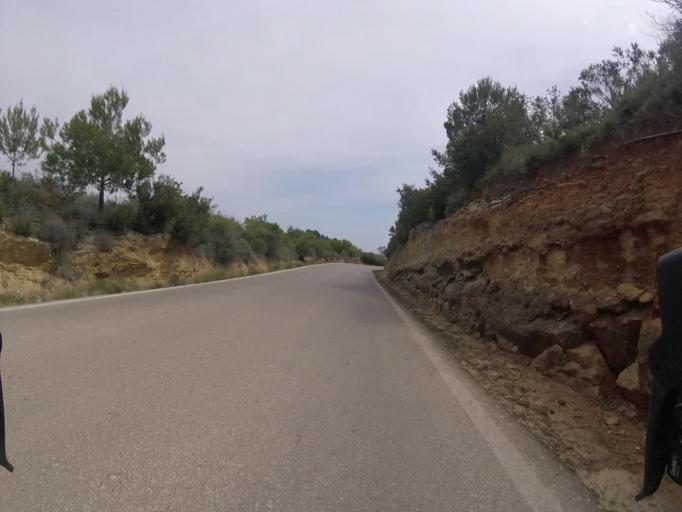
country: ES
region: Valencia
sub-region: Provincia de Castello
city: Cabanes
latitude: 40.1606
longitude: 0.0758
